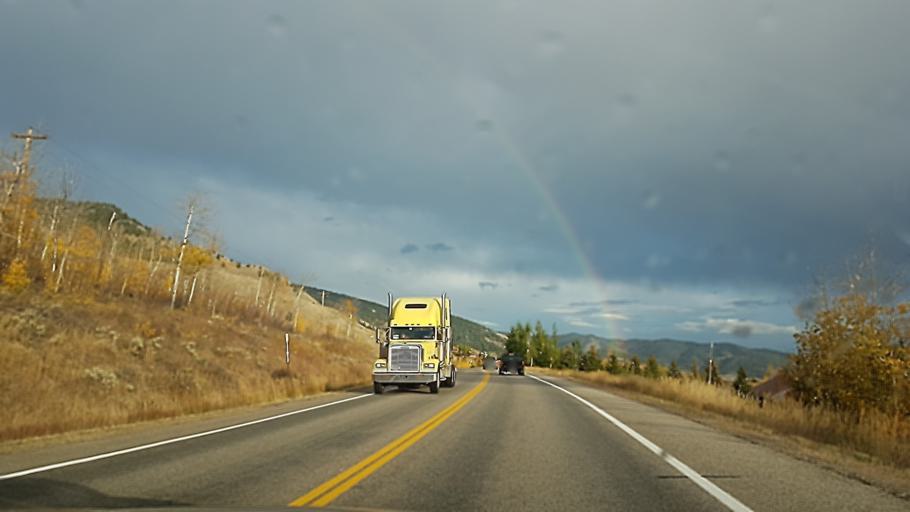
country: US
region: Montana
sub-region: Gallatin County
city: West Yellowstone
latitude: 44.6673
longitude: -111.3957
